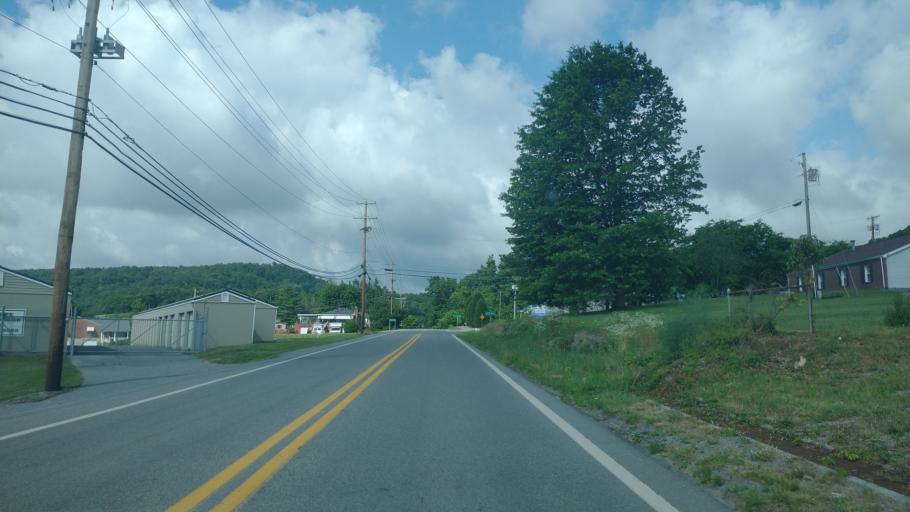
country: US
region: West Virginia
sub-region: Mercer County
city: Princeton
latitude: 37.3632
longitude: -81.1226
